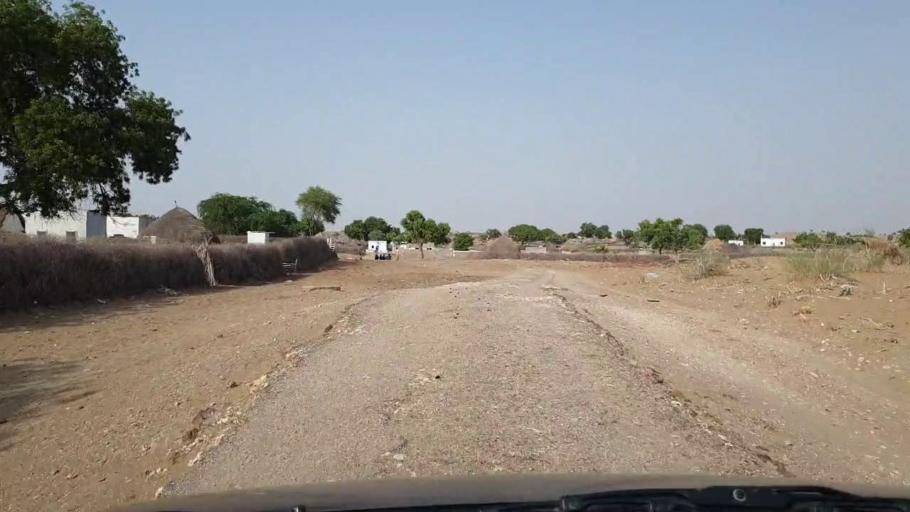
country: PK
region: Sindh
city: Chor
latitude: 25.4558
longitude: 70.5336
